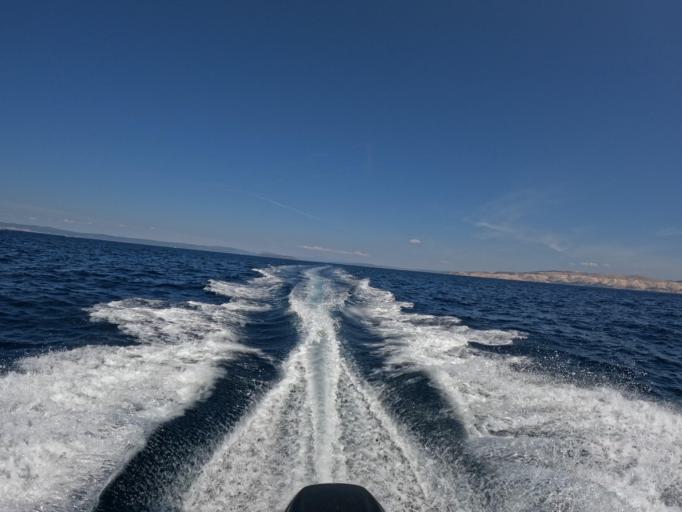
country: HR
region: Primorsko-Goranska
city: Lopar
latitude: 44.8775
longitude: 14.6608
